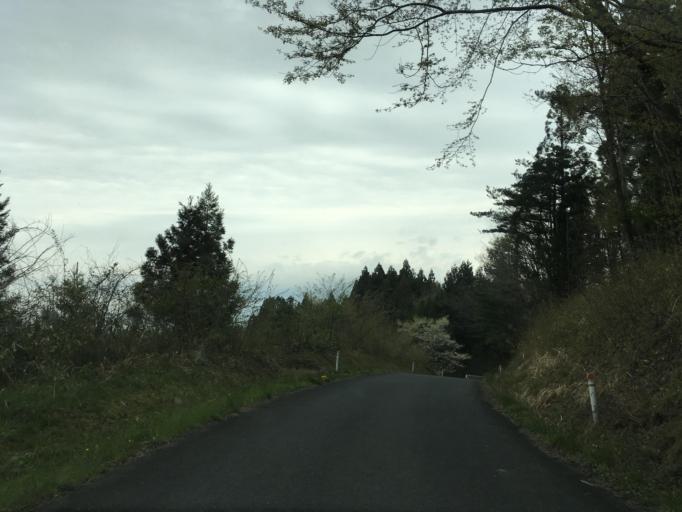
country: JP
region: Iwate
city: Ichinoseki
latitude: 38.8424
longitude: 141.3343
